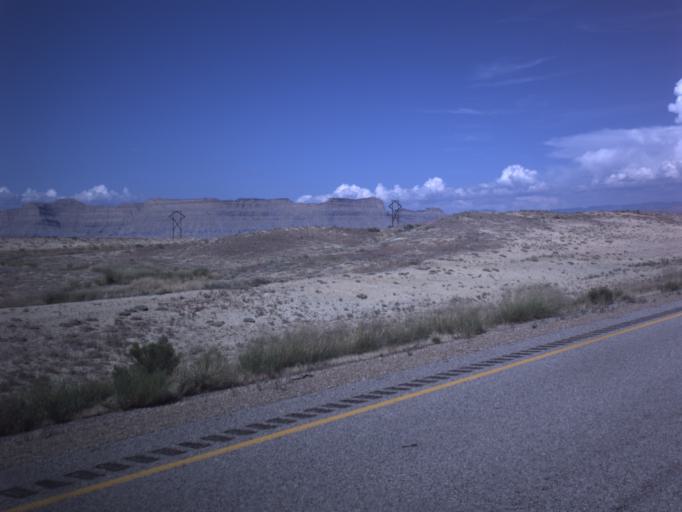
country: US
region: Utah
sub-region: Carbon County
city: East Carbon City
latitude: 38.9644
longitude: -110.2787
